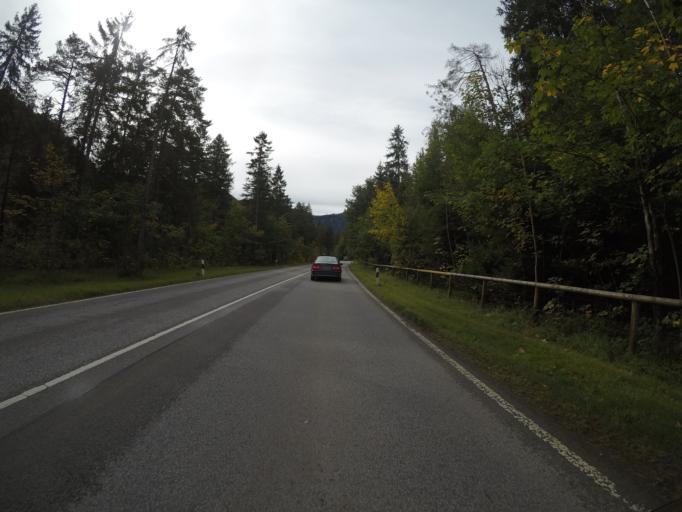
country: DE
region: Bavaria
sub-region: Upper Bavaria
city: Kreuth
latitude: 47.6340
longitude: 11.7460
